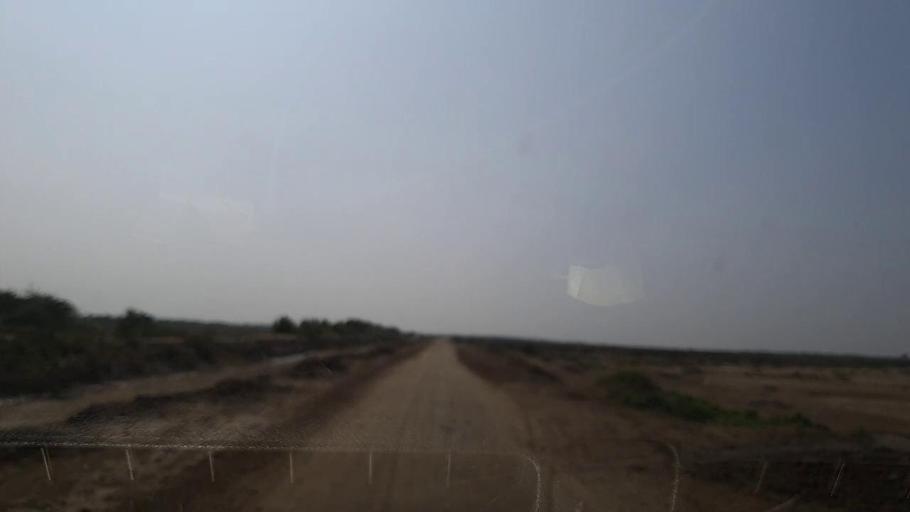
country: PK
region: Sindh
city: Mirpur Sakro
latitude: 24.5446
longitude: 67.7888
